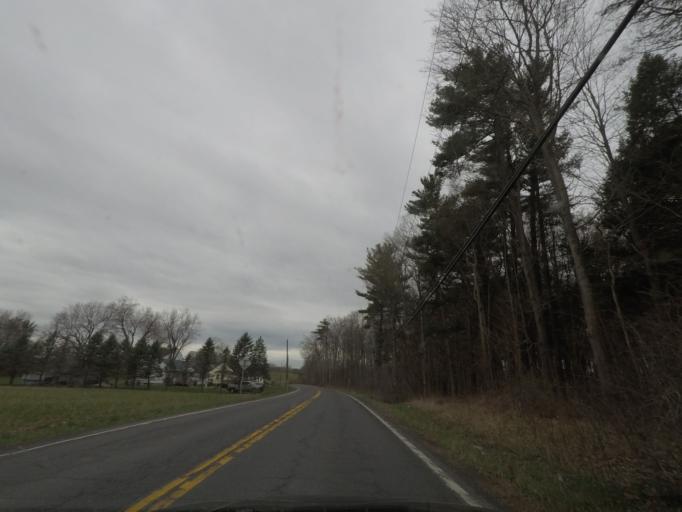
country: US
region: New York
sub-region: Albany County
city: Ravena
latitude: 42.5366
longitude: -73.8309
